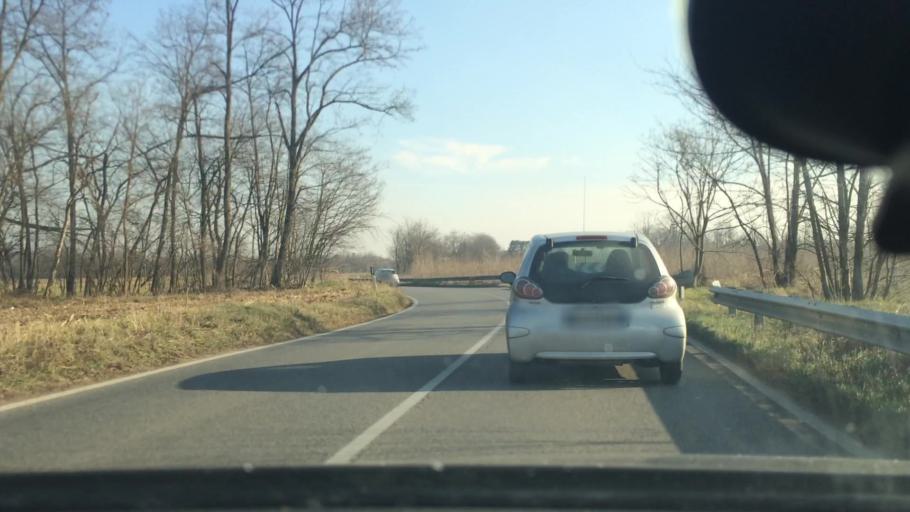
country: IT
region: Lombardy
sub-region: Citta metropolitana di Milano
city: Casorezzo
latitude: 45.5130
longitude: 8.9213
